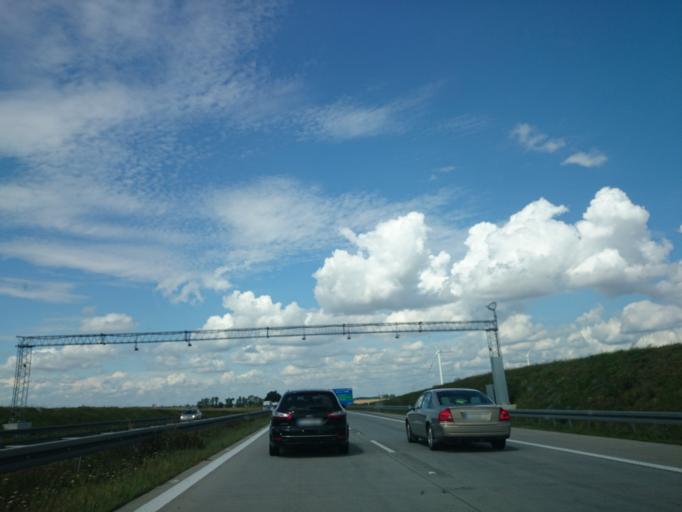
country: PL
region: Lower Silesian Voivodeship
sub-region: Powiat legnicki
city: Legnickie Pole
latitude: 51.1342
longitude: 16.2975
